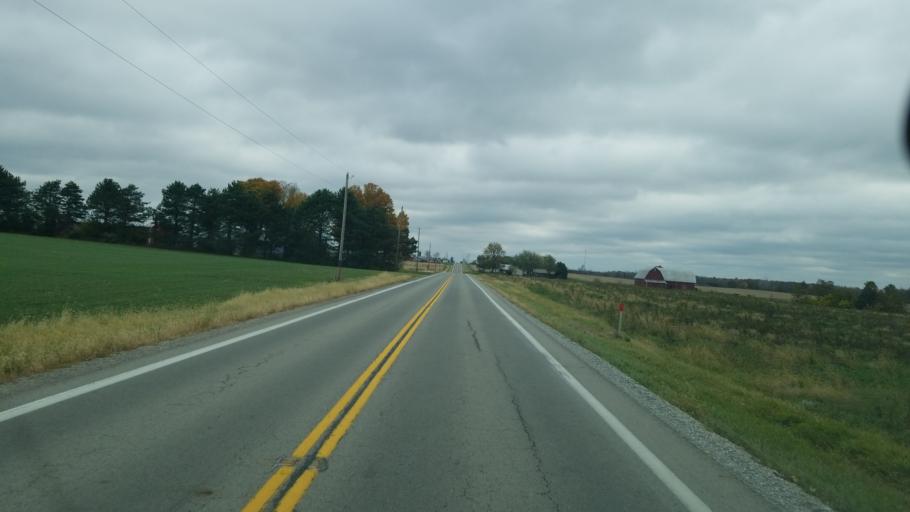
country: US
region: Ohio
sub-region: Sandusky County
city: Mount Carmel
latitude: 41.0810
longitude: -82.9533
